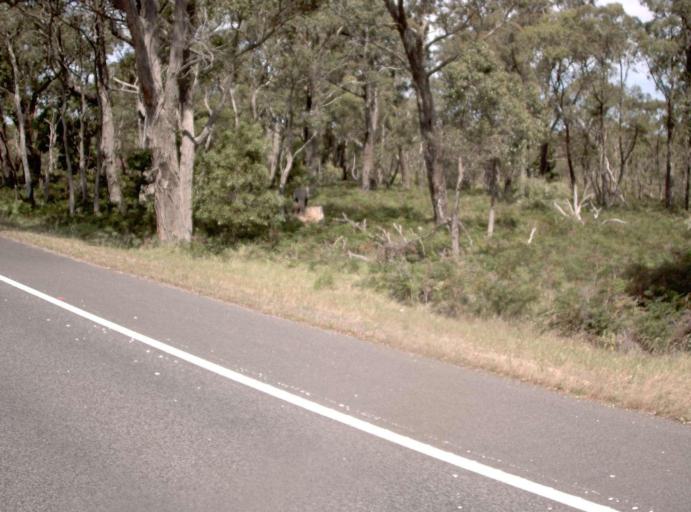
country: AU
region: Victoria
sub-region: East Gippsland
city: Bairnsdale
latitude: -37.9062
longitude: 147.3310
